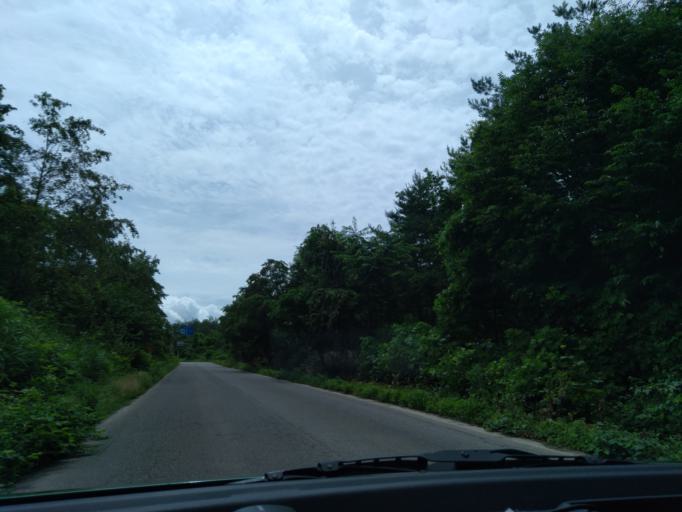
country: JP
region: Akita
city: Kakunodatemachi
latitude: 39.5772
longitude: 140.6285
